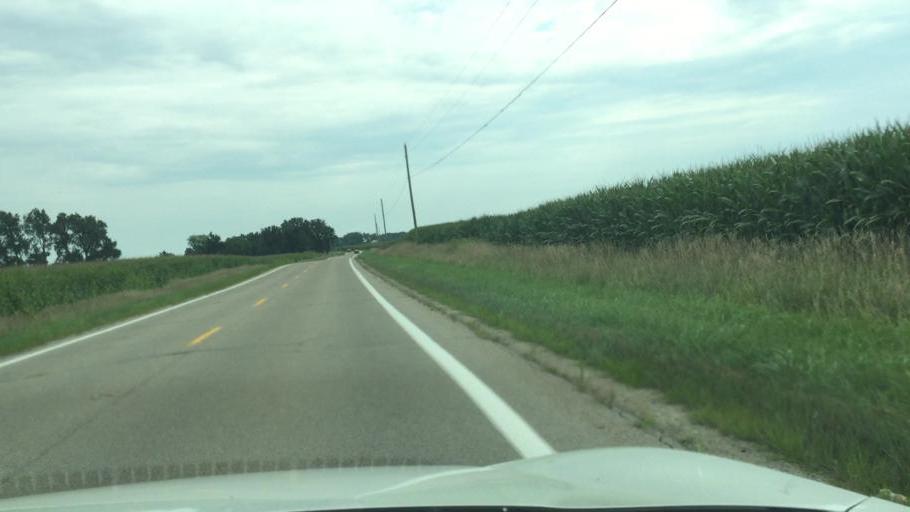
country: US
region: Ohio
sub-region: Champaign County
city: North Lewisburg
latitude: 40.1548
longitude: -83.5281
